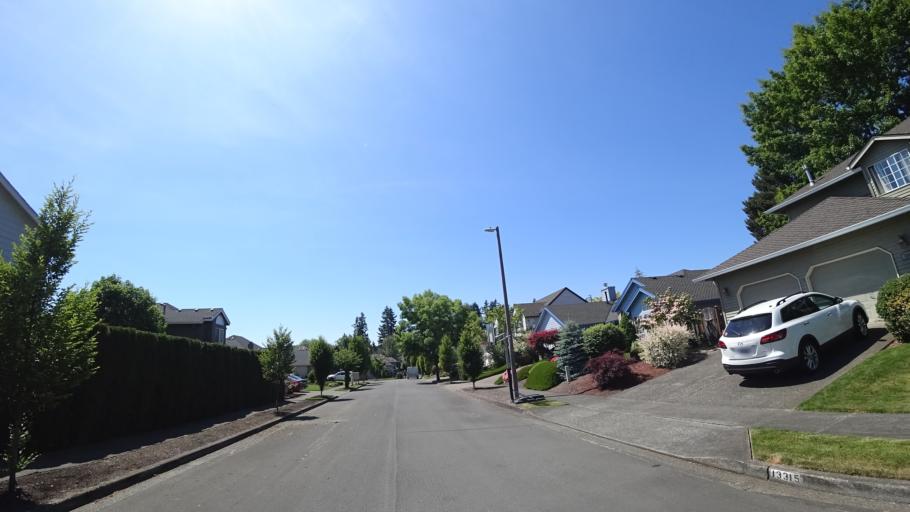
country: US
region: Oregon
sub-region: Washington County
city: Beaverton
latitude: 45.4452
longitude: -122.8139
